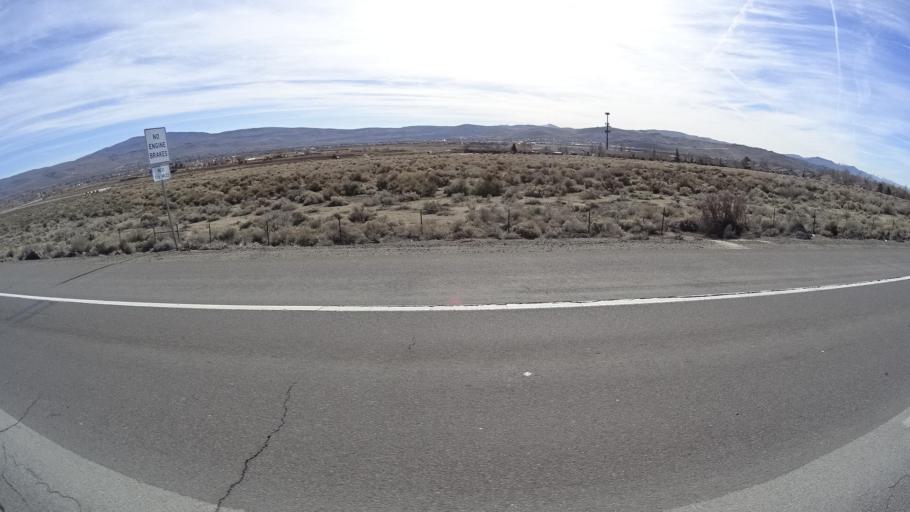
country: US
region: Nevada
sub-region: Washoe County
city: Spanish Springs
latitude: 39.6260
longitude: -119.7218
